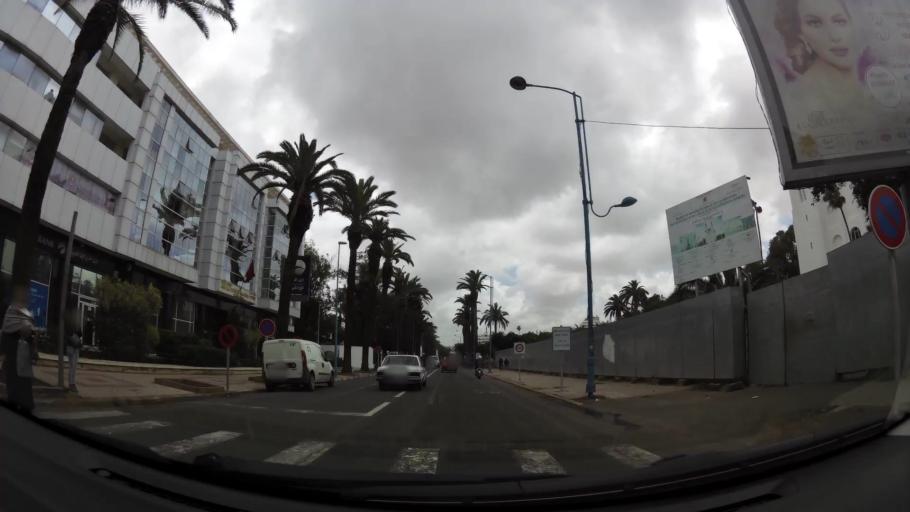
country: MA
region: Grand Casablanca
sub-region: Casablanca
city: Casablanca
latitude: 33.5920
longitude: -7.6245
